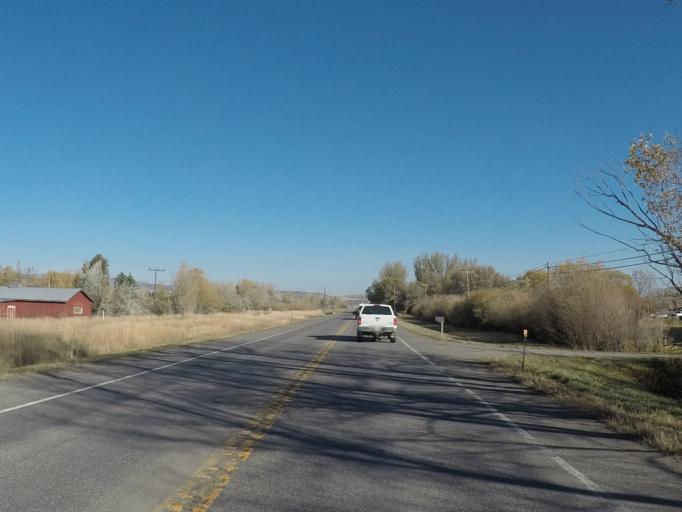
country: US
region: Montana
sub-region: Park County
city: Livingston
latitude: 45.6209
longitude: -110.5787
